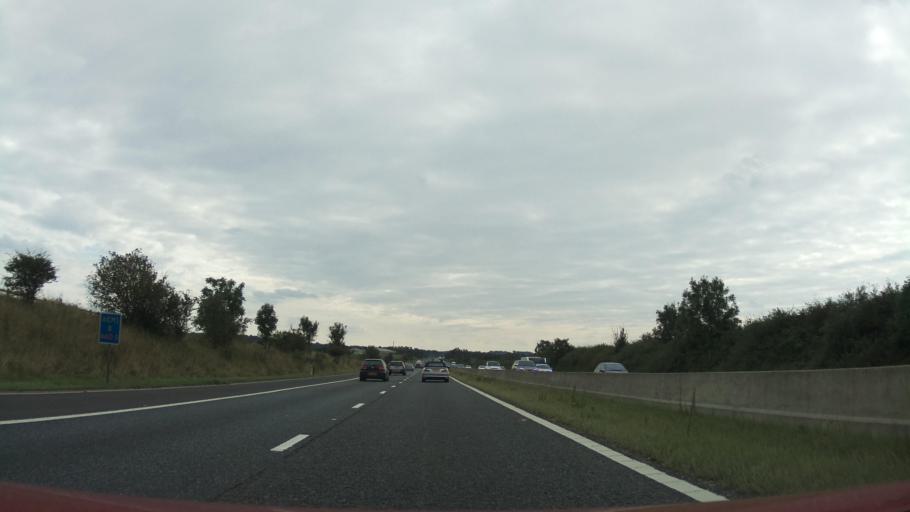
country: GB
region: England
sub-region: County Durham
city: West Rainton
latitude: 54.8266
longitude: -1.5233
